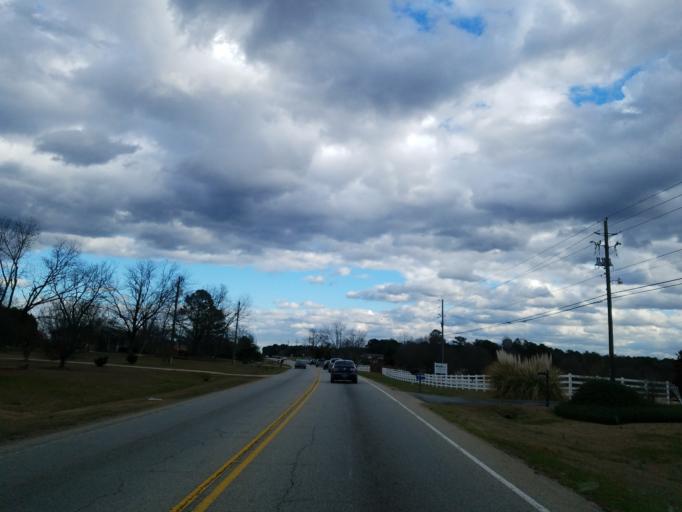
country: US
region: Georgia
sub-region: Henry County
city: McDonough
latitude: 33.4310
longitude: -84.1094
